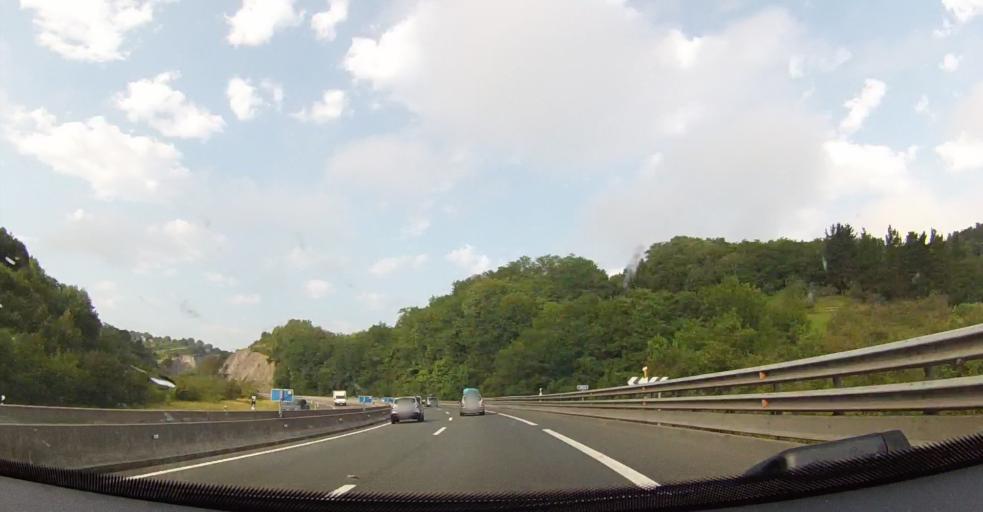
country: ES
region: Basque Country
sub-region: Provincia de Guipuzcoa
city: Zumaia
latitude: 43.2778
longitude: -2.2536
